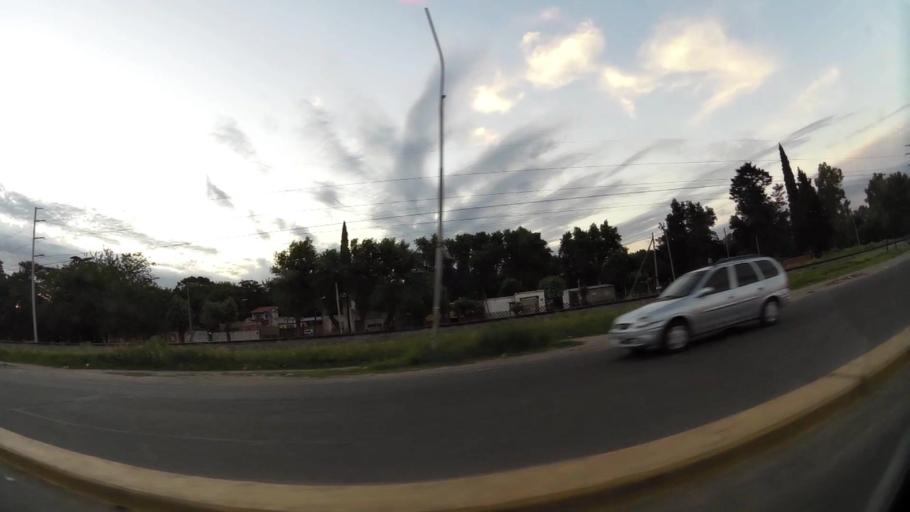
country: AR
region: Buenos Aires
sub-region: Partido de Merlo
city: Merlo
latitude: -34.6886
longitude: -58.7661
